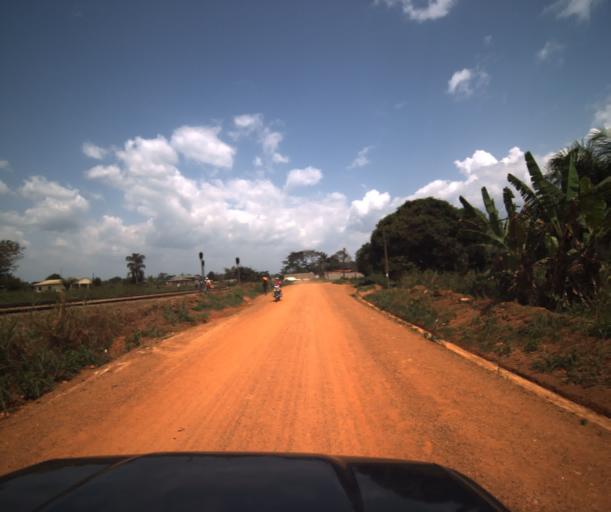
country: CM
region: Centre
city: Eseka
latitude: 3.5470
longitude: 11.0362
